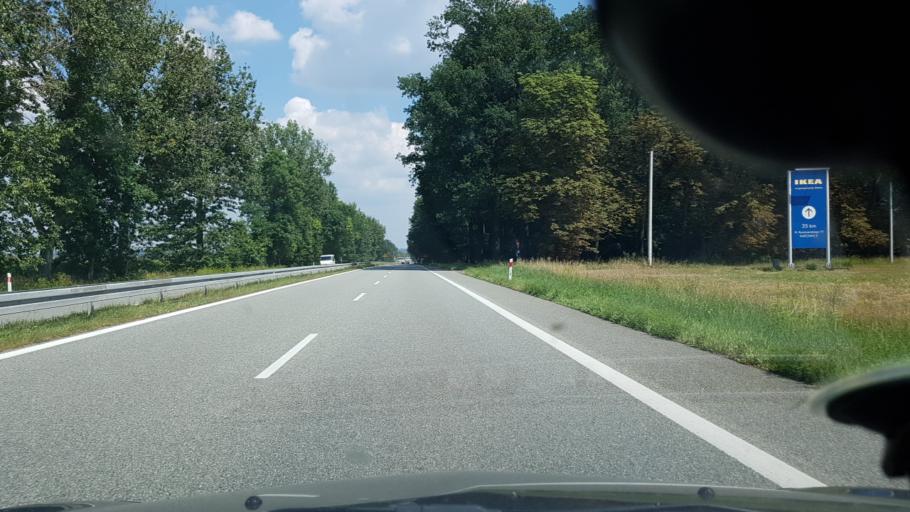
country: PL
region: Silesian Voivodeship
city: Gardawice
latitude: 50.0960
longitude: 18.7706
